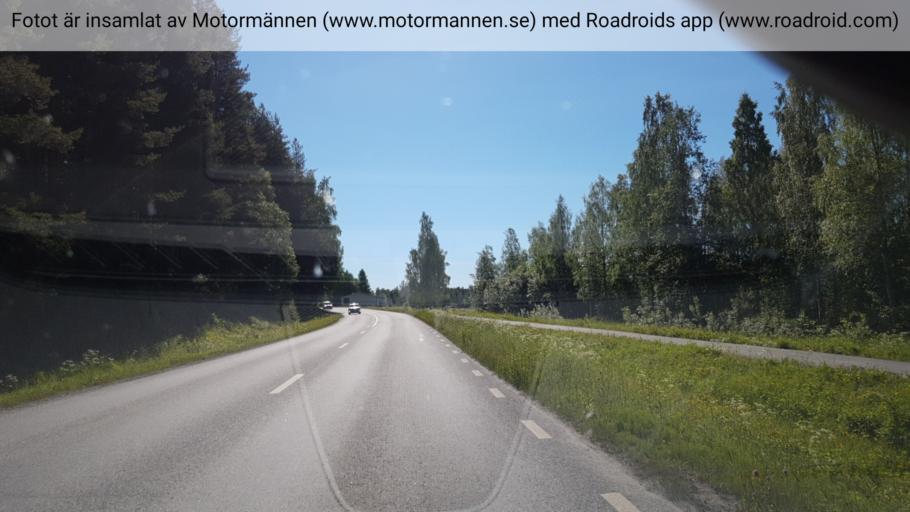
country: SE
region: Norrbotten
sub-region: Bodens Kommun
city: Boden
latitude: 65.8318
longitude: 21.6209
